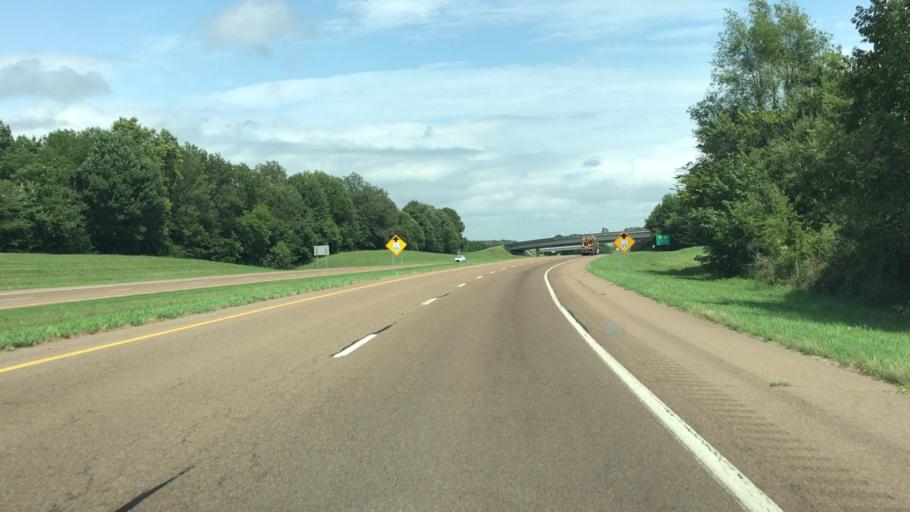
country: US
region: Tennessee
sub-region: Obion County
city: South Fulton
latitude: 36.4947
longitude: -88.9128
